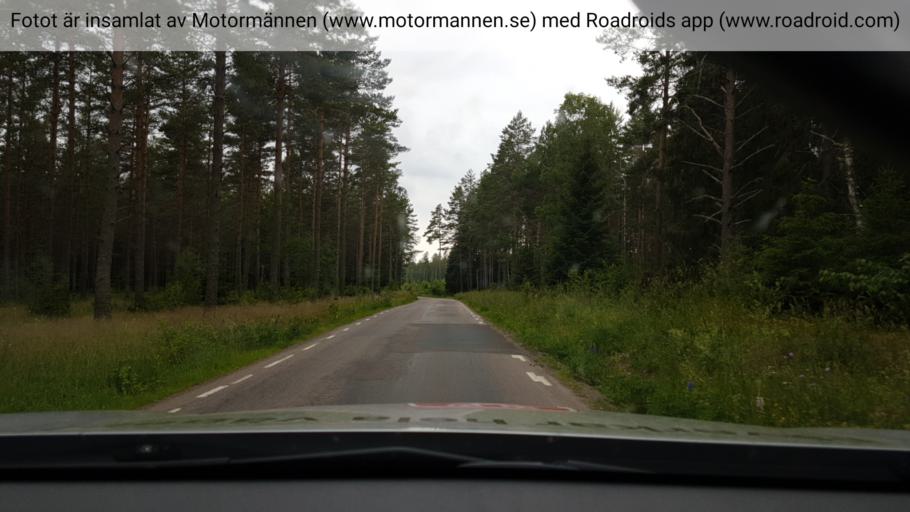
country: SE
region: Vaestra Goetaland
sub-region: Tidaholms Kommun
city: Tidaholm
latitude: 58.0623
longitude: 14.0534
